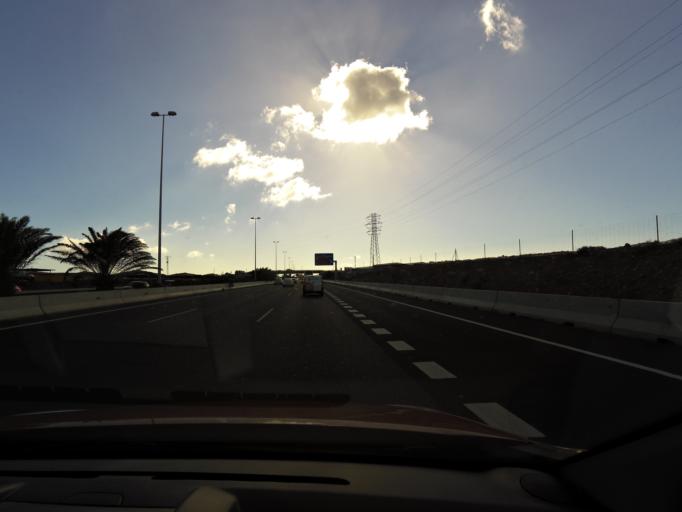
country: ES
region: Canary Islands
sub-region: Provincia de Las Palmas
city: Cruce de Arinaga
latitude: 27.8484
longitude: -15.4340
